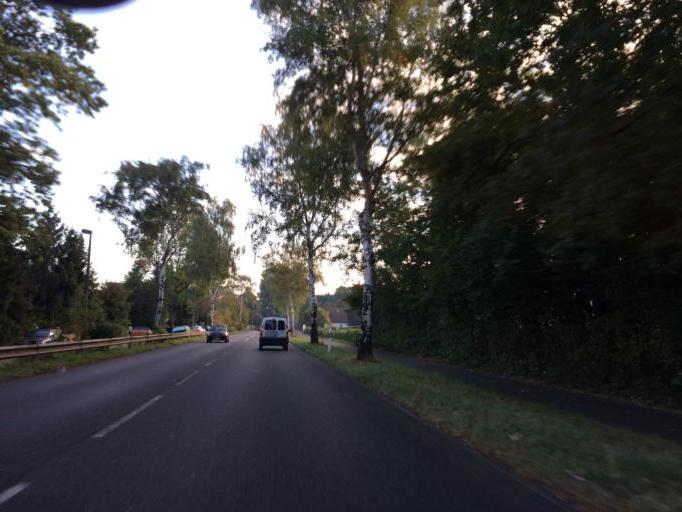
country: DE
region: North Rhine-Westphalia
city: Sankt Augustin
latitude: 50.7544
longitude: 7.1621
